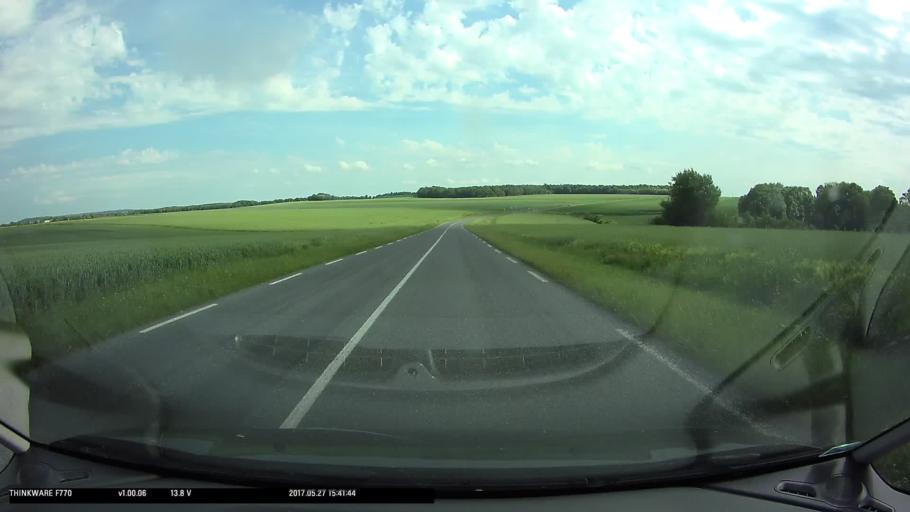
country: FR
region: Picardie
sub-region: Departement de l'Oise
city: Chaumont-en-Vexin
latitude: 49.2264
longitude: 1.8838
